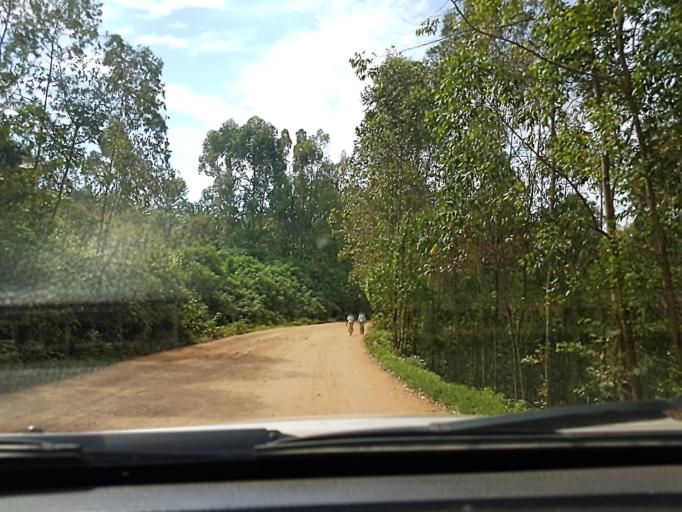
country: CD
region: South Kivu
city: Bukavu
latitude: -2.6226
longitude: 28.8773
